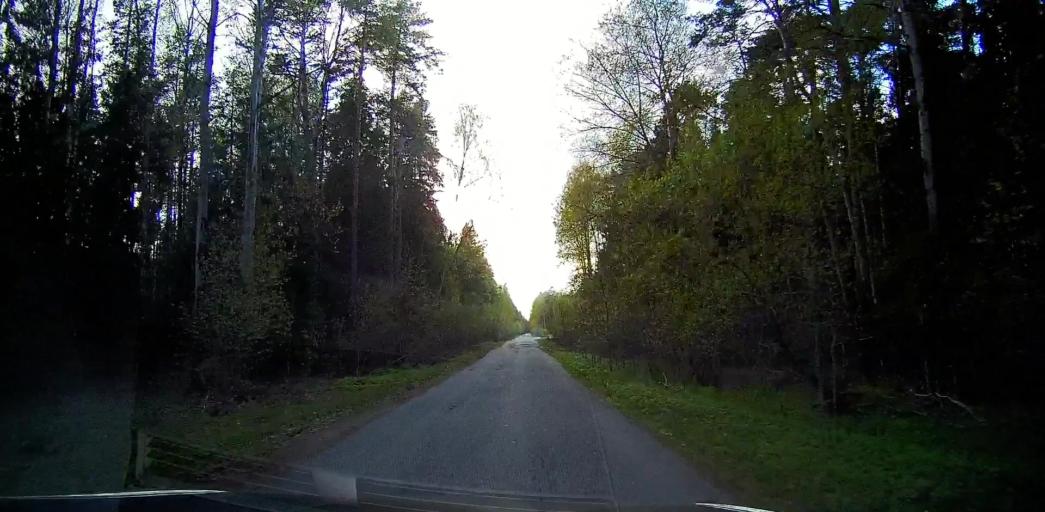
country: RU
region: Moskovskaya
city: Malyshevo
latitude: 55.5504
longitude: 38.3553
